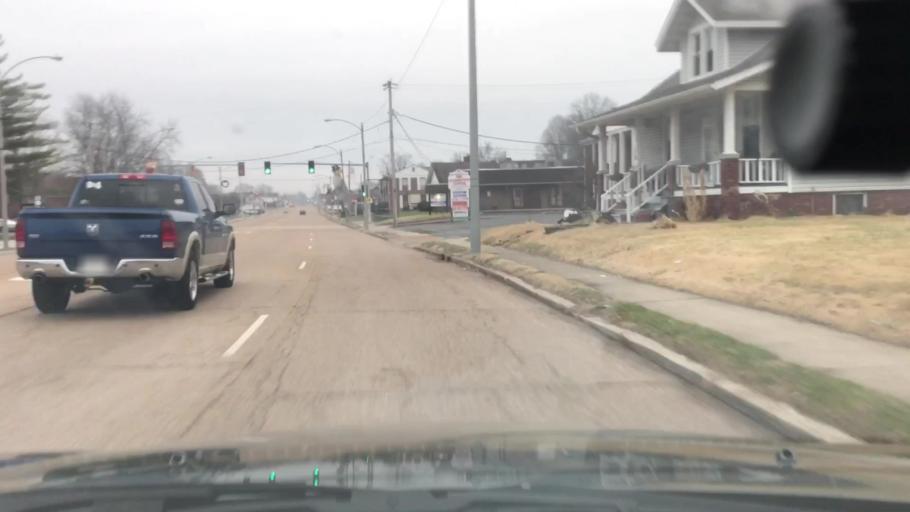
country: US
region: Illinois
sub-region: Saint Clair County
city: Swansea
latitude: 38.5466
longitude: -90.0326
